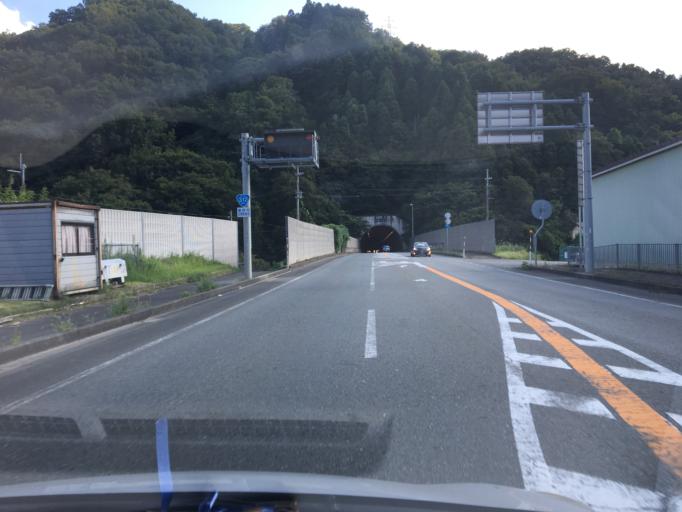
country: JP
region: Hyogo
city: Toyooka
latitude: 35.4660
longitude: 134.7683
